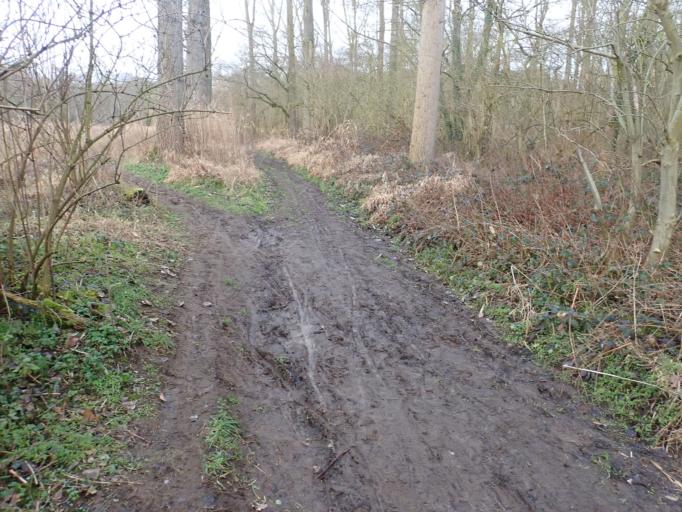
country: BE
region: Flanders
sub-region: Provincie Vlaams-Brabant
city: Tremelo
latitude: 50.9818
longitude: 4.6956
